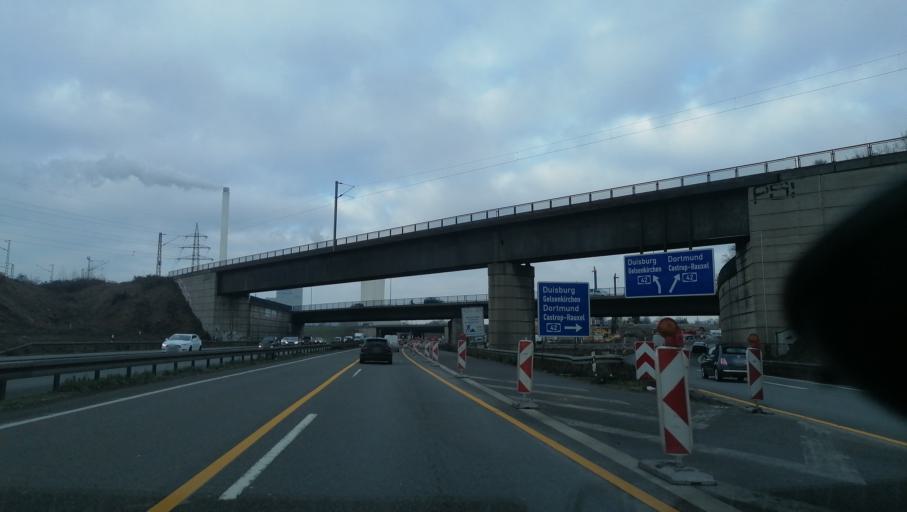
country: DE
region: North Rhine-Westphalia
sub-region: Regierungsbezirk Arnsberg
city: Herne
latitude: 51.5422
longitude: 7.2046
